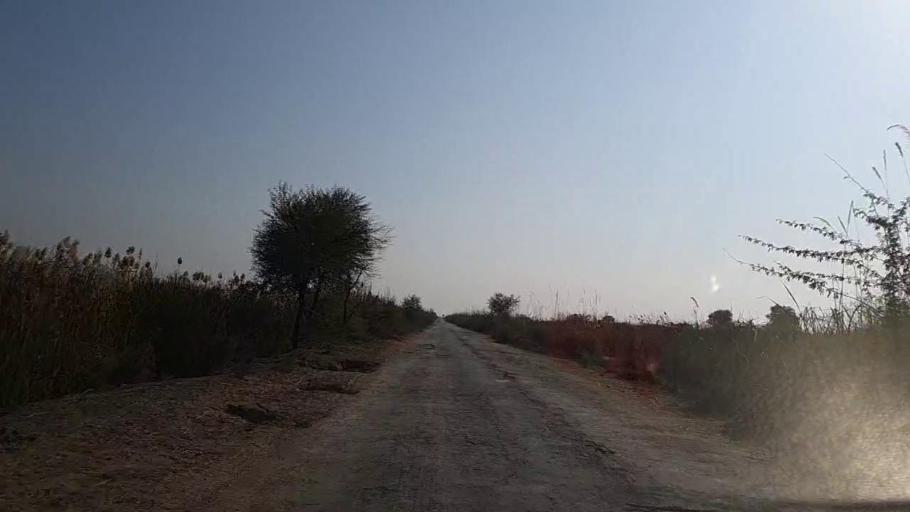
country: PK
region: Sindh
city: Tando Mittha Khan
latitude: 25.8954
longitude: 69.0770
